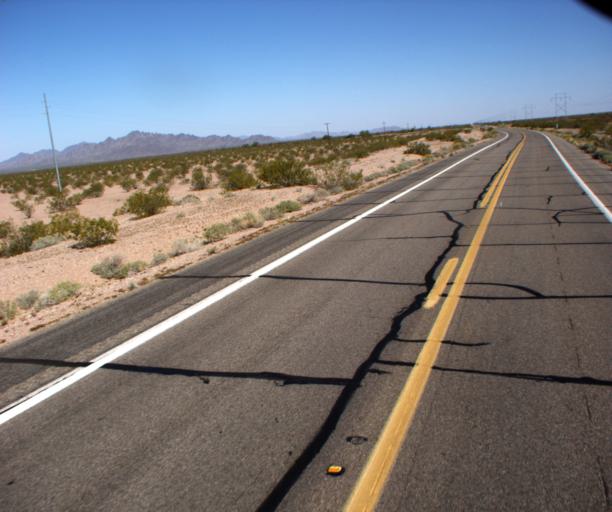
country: US
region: Arizona
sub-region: La Paz County
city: Quartzsite
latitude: 33.4112
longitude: -114.2171
